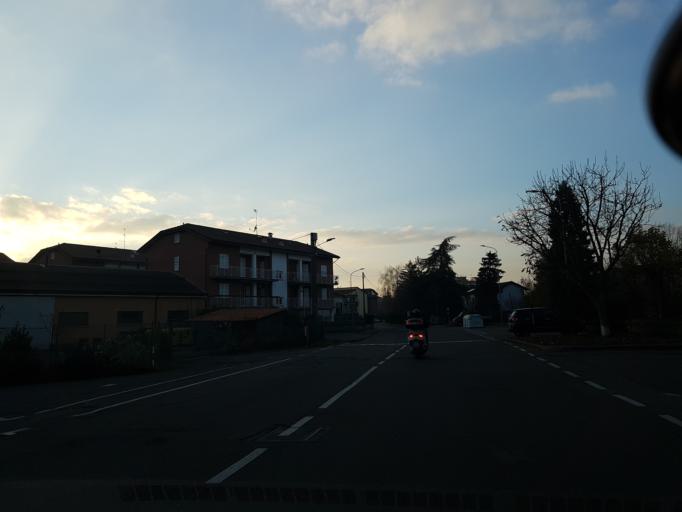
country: IT
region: Piedmont
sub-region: Provincia di Alessandria
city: Novi Ligure
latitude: 44.7585
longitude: 8.8024
